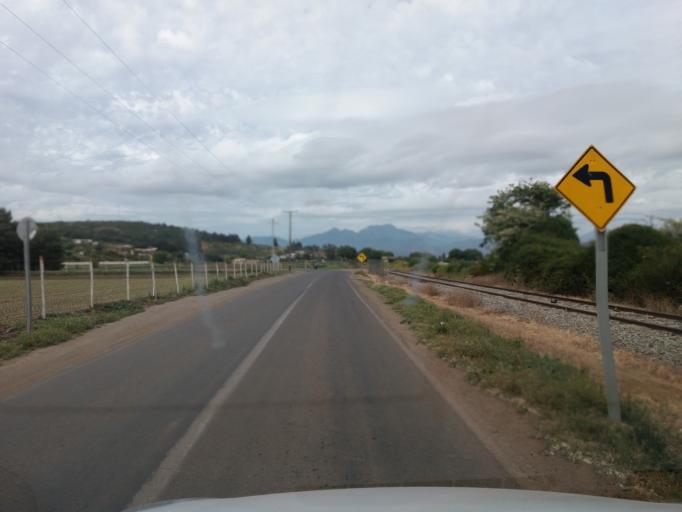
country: CL
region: Valparaiso
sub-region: Provincia de Marga Marga
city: Villa Alemana
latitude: -32.9173
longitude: -71.3963
